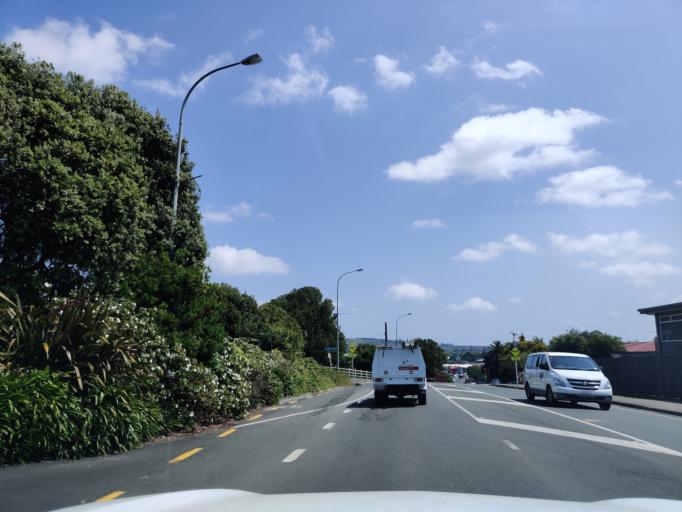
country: NZ
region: Auckland
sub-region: Auckland
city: Pukekohe East
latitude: -37.1991
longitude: 174.9108
